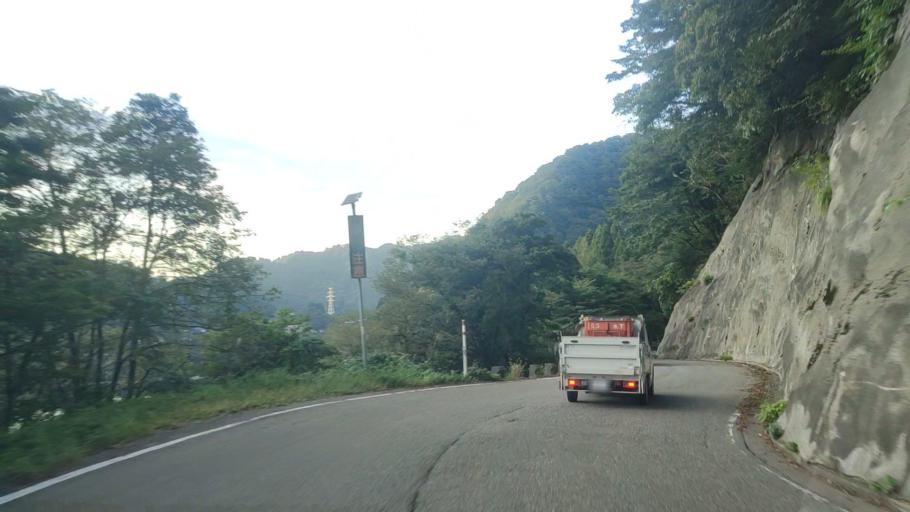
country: JP
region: Toyama
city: Nanto-shi
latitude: 36.5542
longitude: 137.0113
